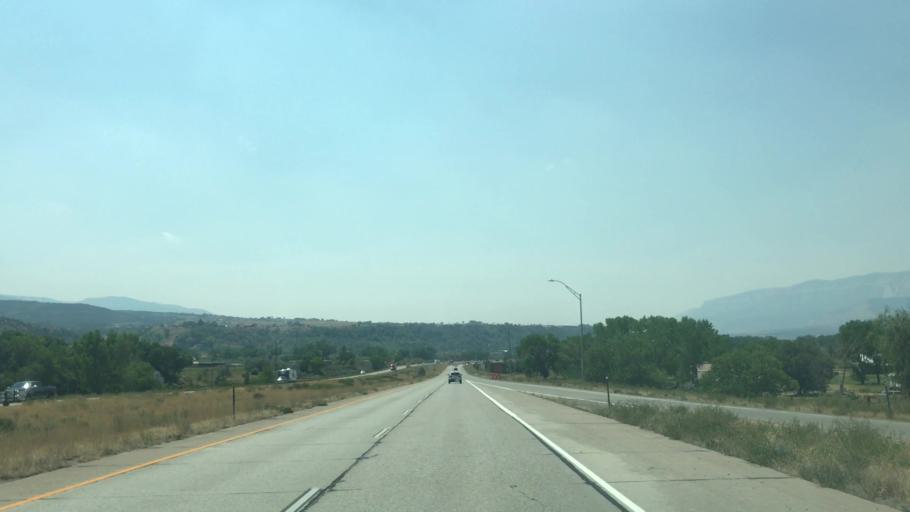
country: US
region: Colorado
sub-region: Garfield County
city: Rifle
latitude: 39.5234
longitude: -107.7803
